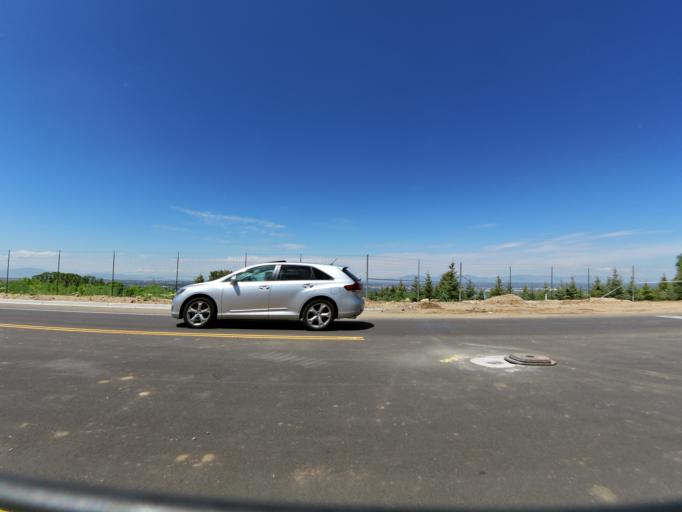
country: US
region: Utah
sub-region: Weber County
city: Uintah
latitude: 41.1816
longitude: -111.9331
